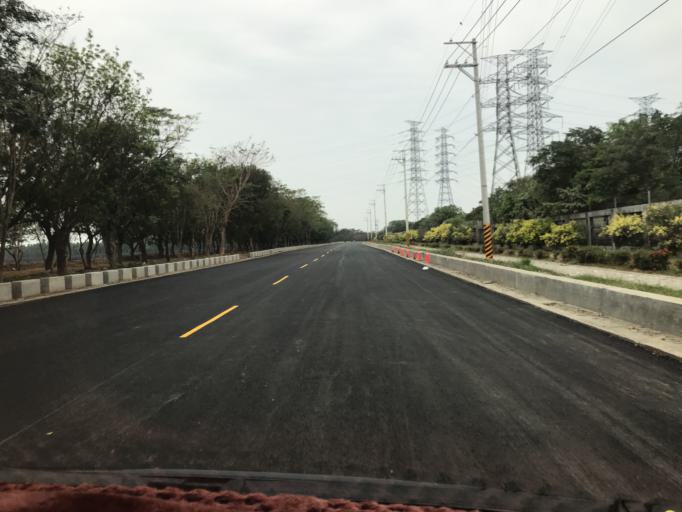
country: TW
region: Taiwan
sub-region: Pingtung
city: Pingtung
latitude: 22.4172
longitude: 120.6077
